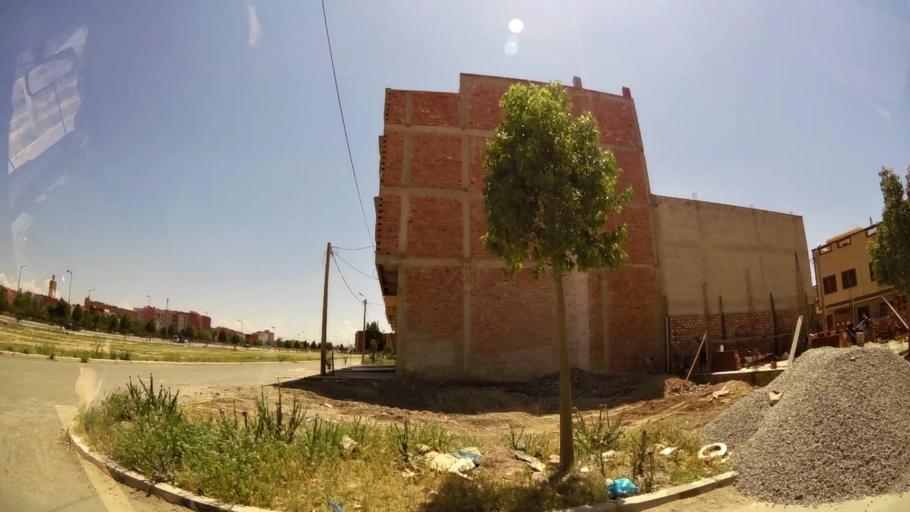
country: MA
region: Oriental
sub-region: Oujda-Angad
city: Oujda
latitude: 34.6854
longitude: -1.9461
